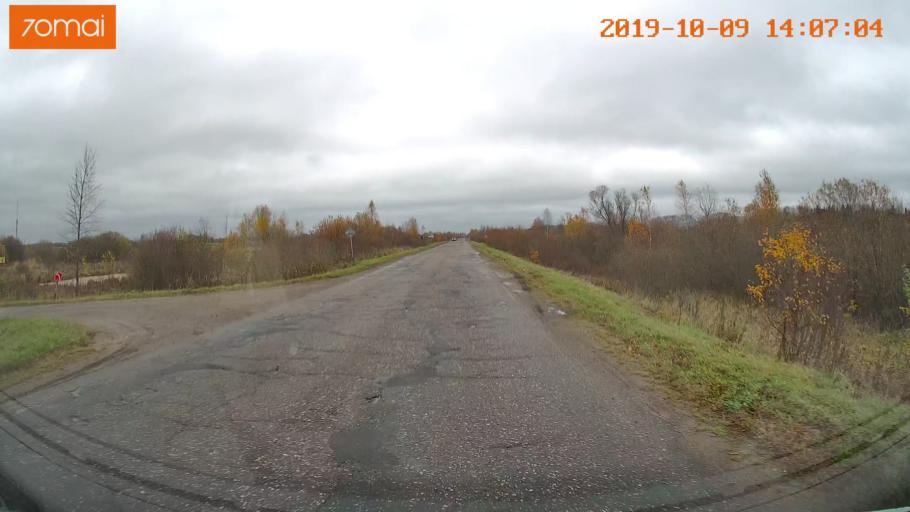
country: RU
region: Kostroma
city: Buy
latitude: 58.4682
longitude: 41.4181
